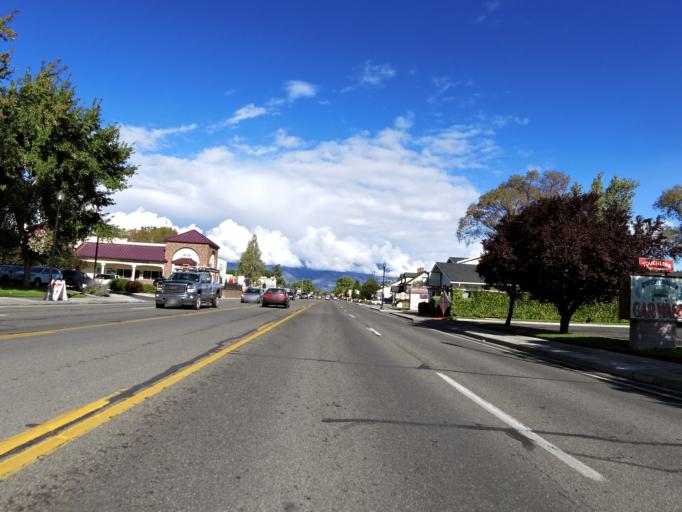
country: US
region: Nevada
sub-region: Douglas County
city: Gardnerville
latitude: 38.9445
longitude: -119.7533
